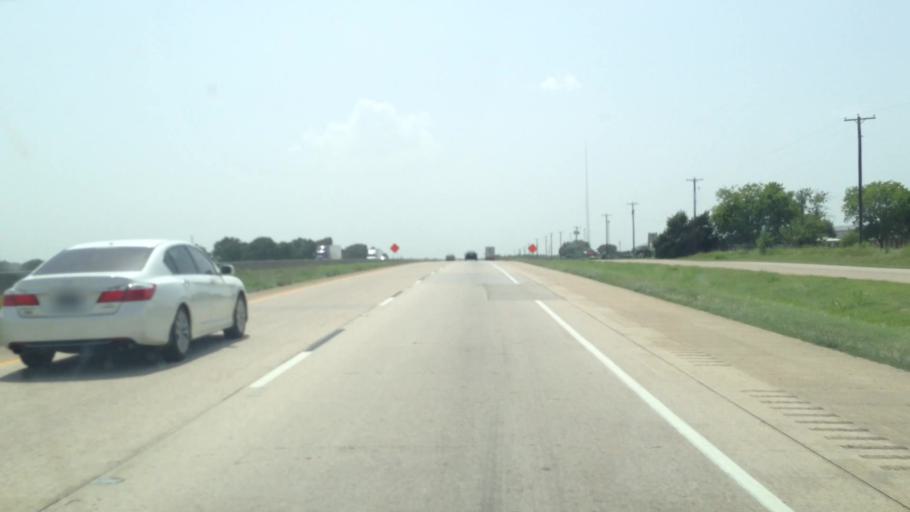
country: US
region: Texas
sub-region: Hopkins County
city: Sulphur Springs
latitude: 33.1209
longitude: -95.6986
